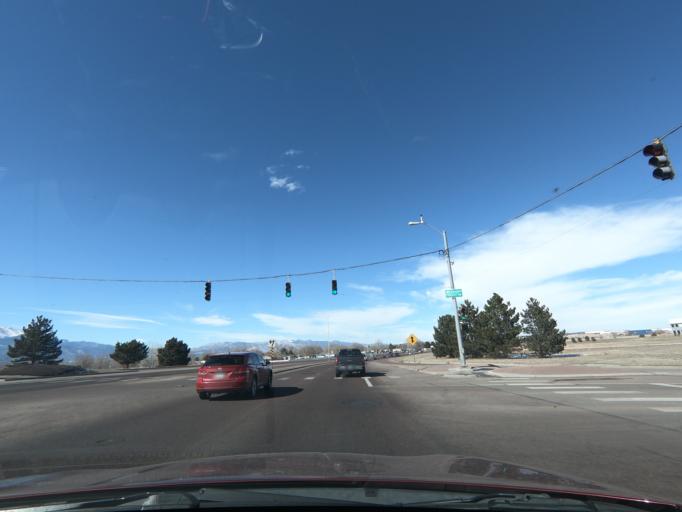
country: US
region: Colorado
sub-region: El Paso County
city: Security-Widefield
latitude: 38.7890
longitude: -104.7289
